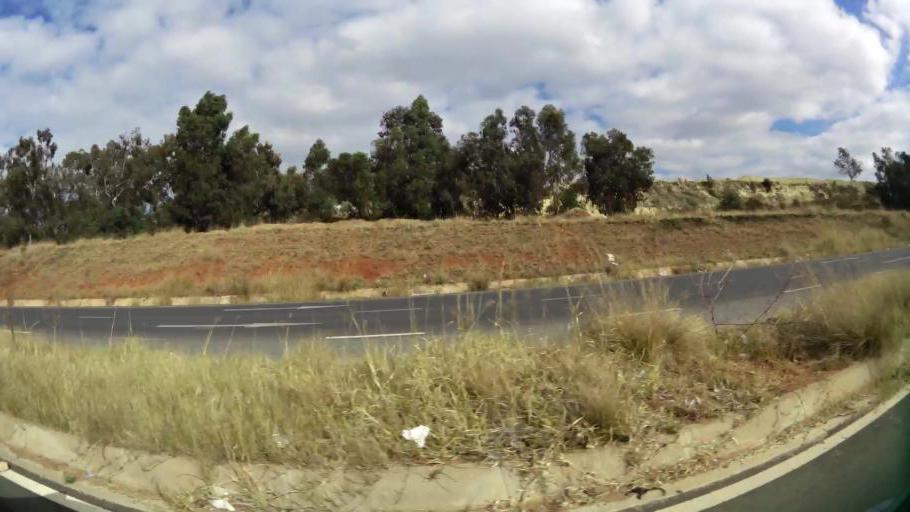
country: ZA
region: Gauteng
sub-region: City of Johannesburg Metropolitan Municipality
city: Roodepoort
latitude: -26.1993
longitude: 27.9031
